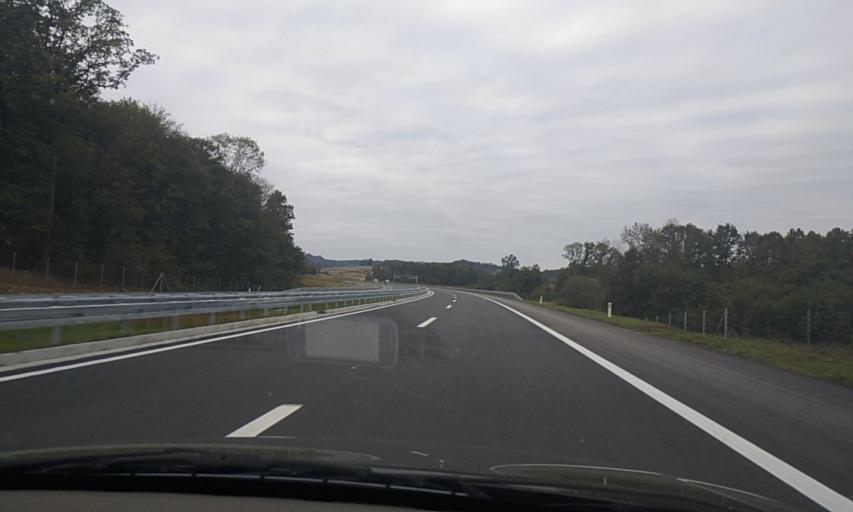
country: BA
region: Republika Srpska
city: Maglajani
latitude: 44.8615
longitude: 17.4744
